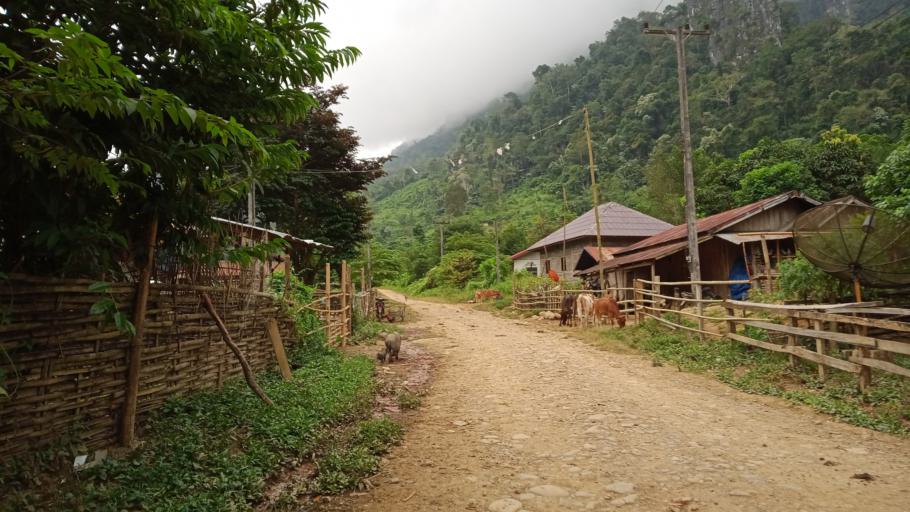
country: LA
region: Xiangkhoang
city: Phonsavan
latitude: 19.0830
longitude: 103.0121
